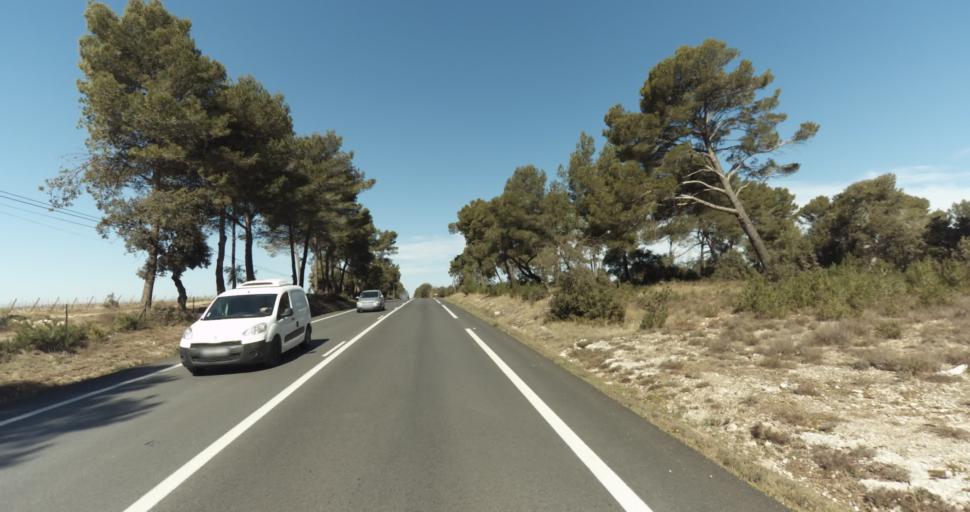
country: FR
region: Provence-Alpes-Cote d'Azur
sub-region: Departement des Bouches-du-Rhone
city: Eguilles
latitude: 43.6014
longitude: 5.3443
